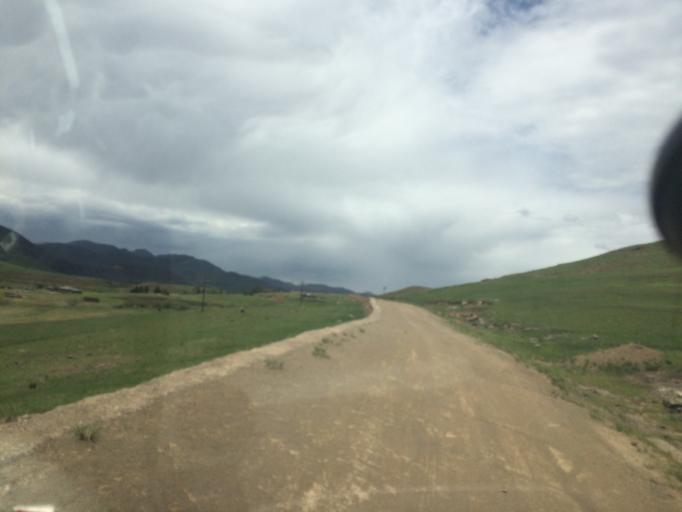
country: LS
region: Maseru
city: Nako
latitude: -29.8592
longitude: 28.0369
